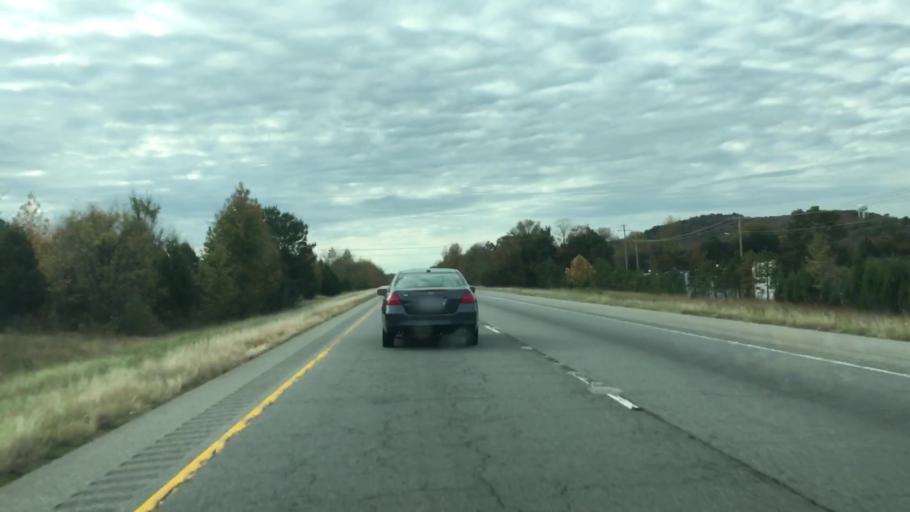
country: US
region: Arkansas
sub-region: Faulkner County
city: Conway
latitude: 35.1198
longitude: -92.4700
